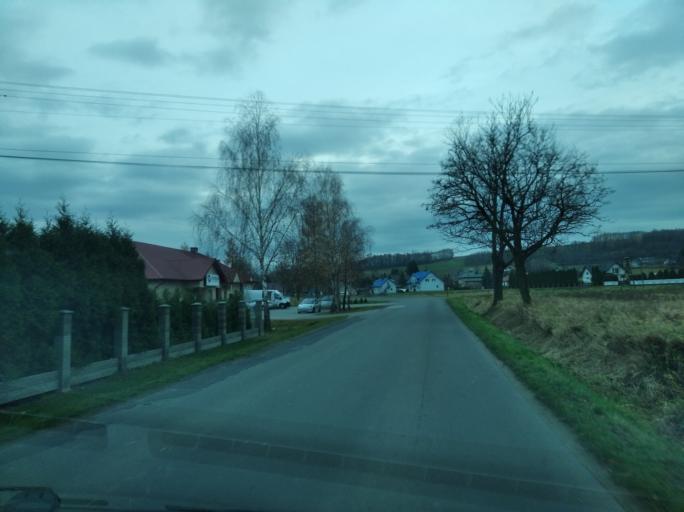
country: PL
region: Subcarpathian Voivodeship
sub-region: Powiat ropczycko-sedziszowski
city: Iwierzyce
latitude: 50.0362
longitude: 21.7463
